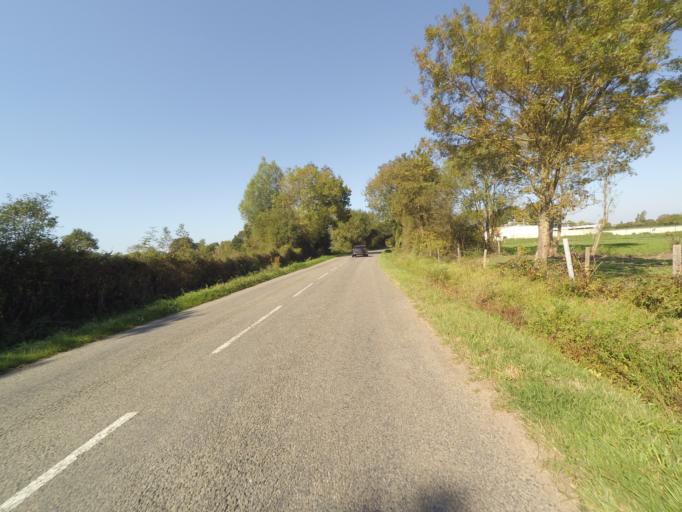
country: FR
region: Pays de la Loire
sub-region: Departement de la Loire-Atlantique
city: Chemere
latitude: 47.1169
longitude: -1.9052
